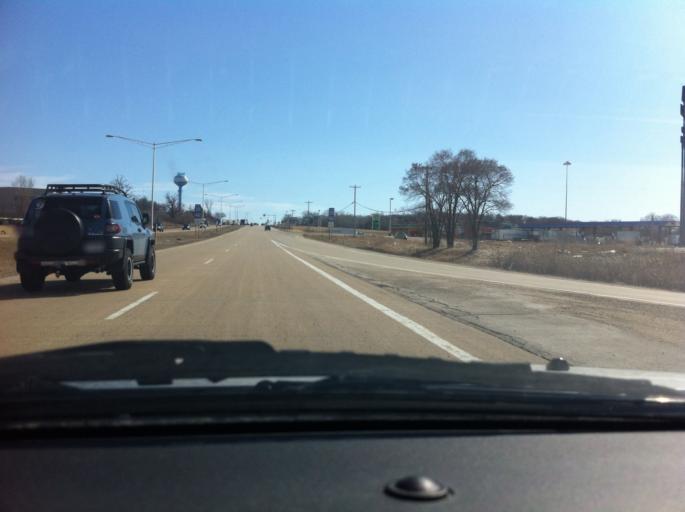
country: US
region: Wisconsin
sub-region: Dane County
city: Windsor
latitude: 43.1764
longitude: -89.3246
